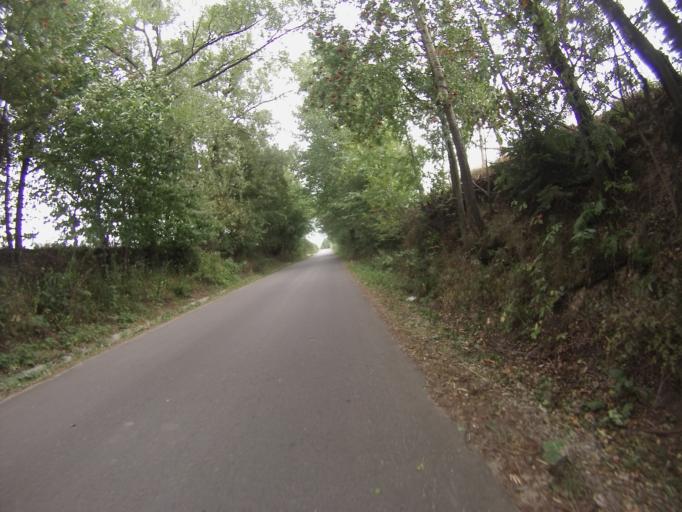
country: PL
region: Swietokrzyskie
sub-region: Powiat kielecki
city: Lagow
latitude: 50.7422
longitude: 21.0522
